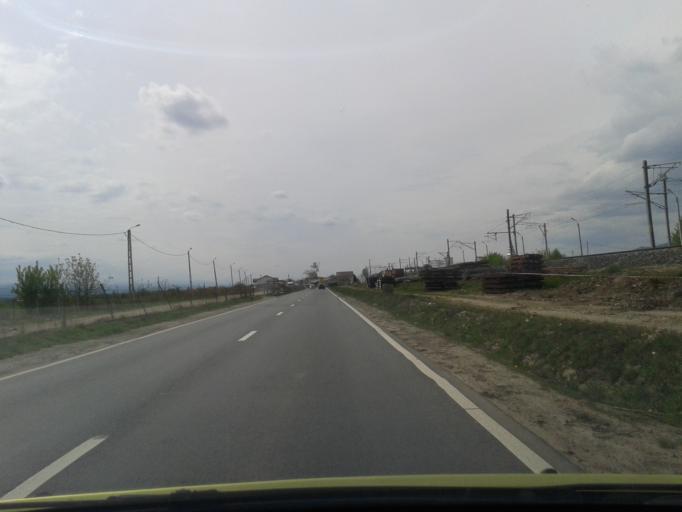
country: RO
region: Alba
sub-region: Municipiul Alba Iulia
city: Alba Iulia
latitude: 46.0629
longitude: 23.5873
